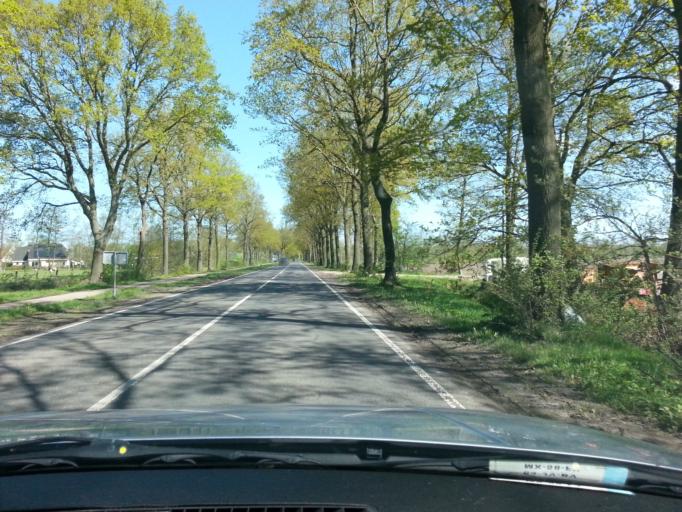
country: NL
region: Friesland
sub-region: Gemeente Achtkarspelen
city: Surhuizum
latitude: 53.1998
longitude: 6.1837
